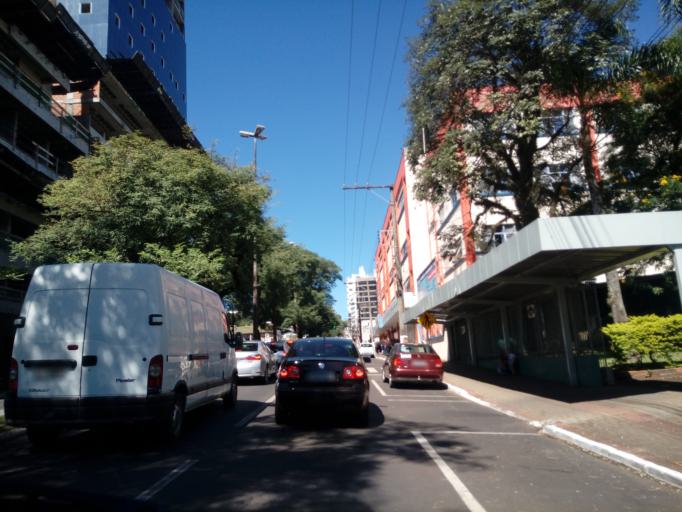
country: BR
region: Santa Catarina
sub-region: Chapeco
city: Chapeco
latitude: -27.1057
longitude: -52.6162
